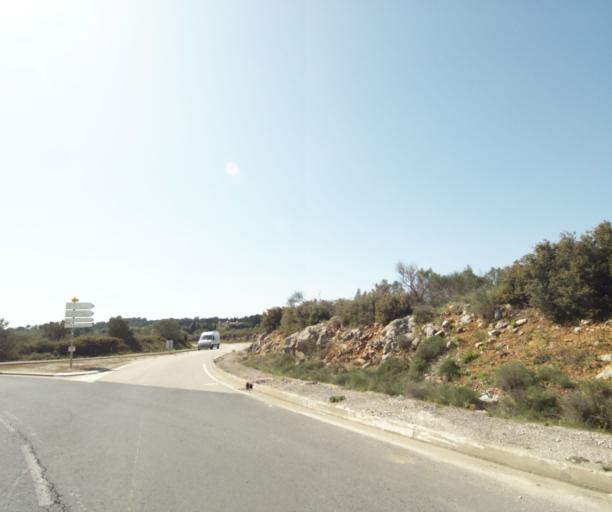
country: FR
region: Languedoc-Roussillon
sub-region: Departement de l'Herault
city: Combaillaux
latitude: 43.6365
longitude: 3.7588
